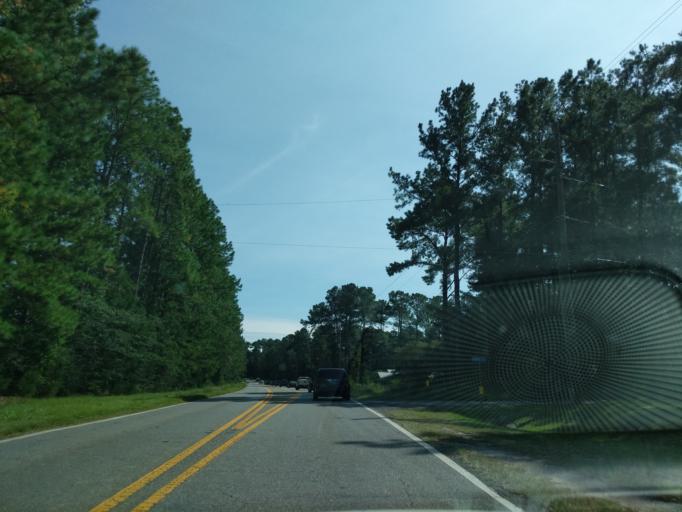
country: US
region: Florida
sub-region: Okaloosa County
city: Crestview
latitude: 30.7344
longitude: -86.6228
